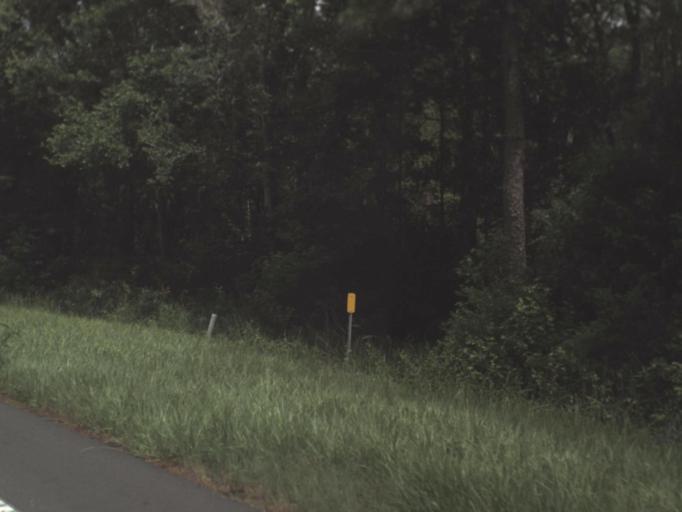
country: US
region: Florida
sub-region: Jefferson County
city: Monticello
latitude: 30.4920
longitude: -83.7138
